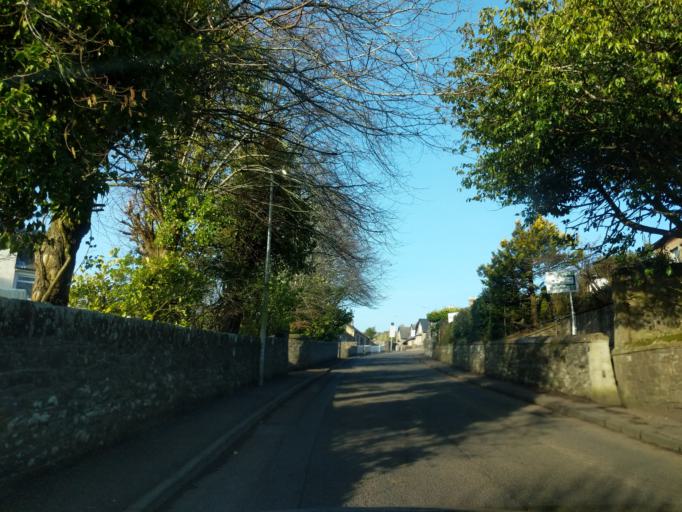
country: GB
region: Scotland
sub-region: South Lanarkshire
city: Lanark
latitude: 55.6690
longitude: -3.7758
